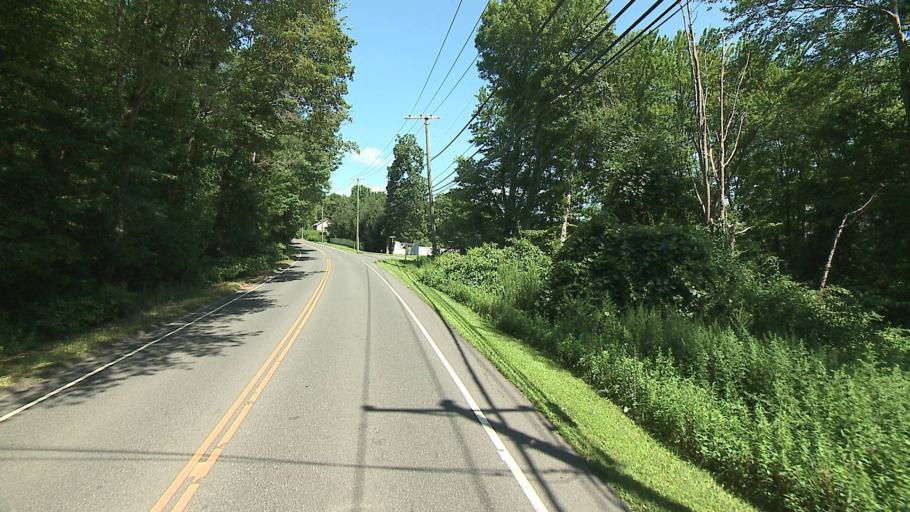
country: US
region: Connecticut
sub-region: New Haven County
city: Oxford
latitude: 41.3653
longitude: -73.1917
